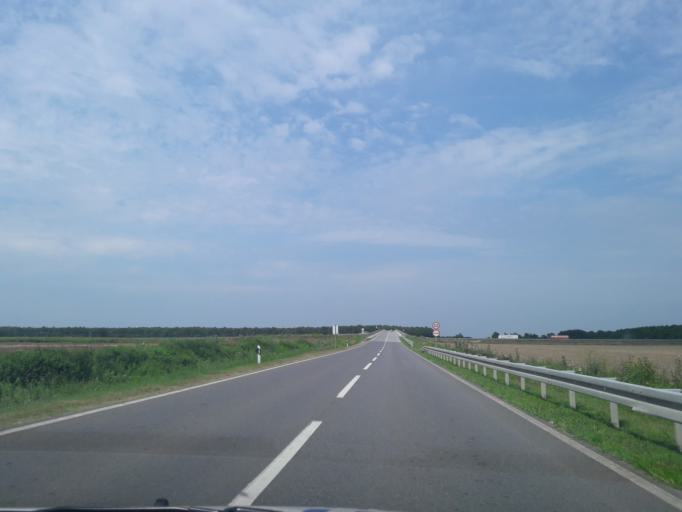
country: HR
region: Osjecko-Baranjska
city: Cepin
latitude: 45.5159
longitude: 18.5149
